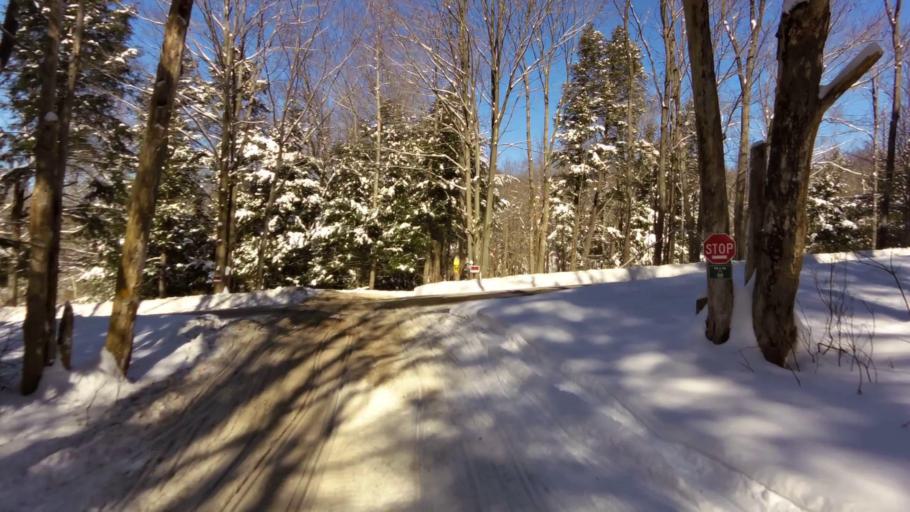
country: US
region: New York
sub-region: Chautauqua County
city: Mayville
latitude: 42.2389
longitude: -79.4231
